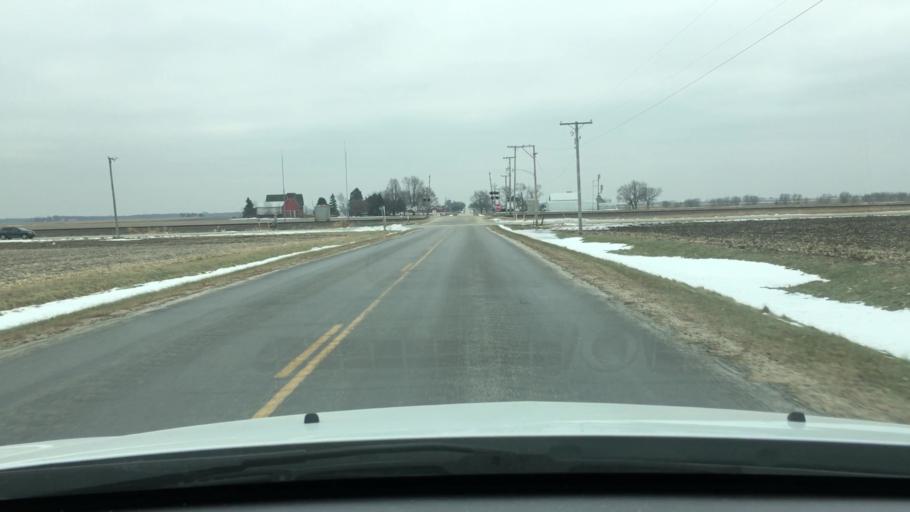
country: US
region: Illinois
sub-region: DeKalb County
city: Waterman
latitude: 41.7706
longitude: -88.7153
